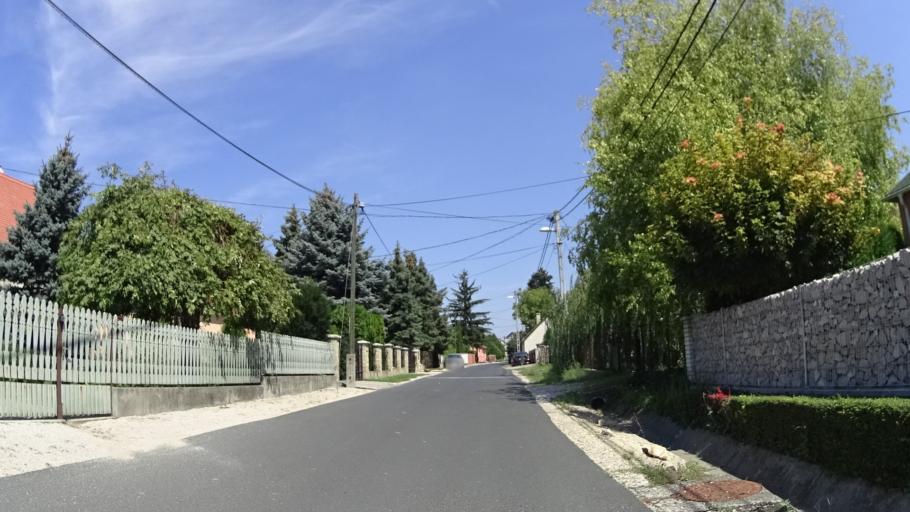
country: HU
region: Fejer
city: Szekesfehervar
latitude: 47.1915
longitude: 18.4534
